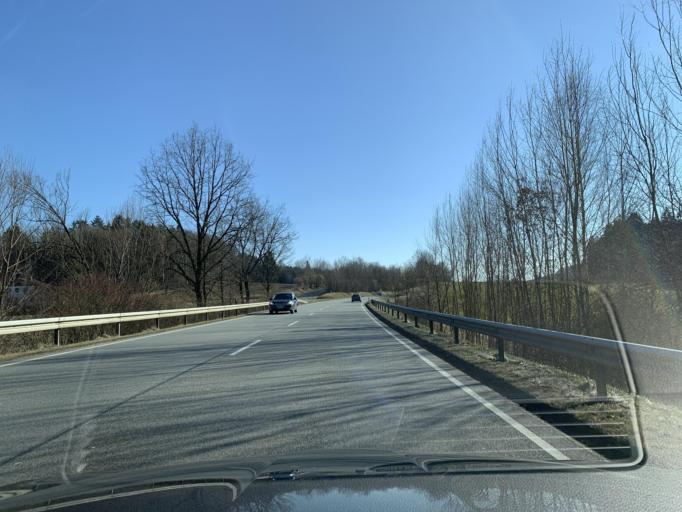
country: DE
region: Bavaria
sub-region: Upper Palatinate
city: Schonthal
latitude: 49.3231
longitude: 12.6340
